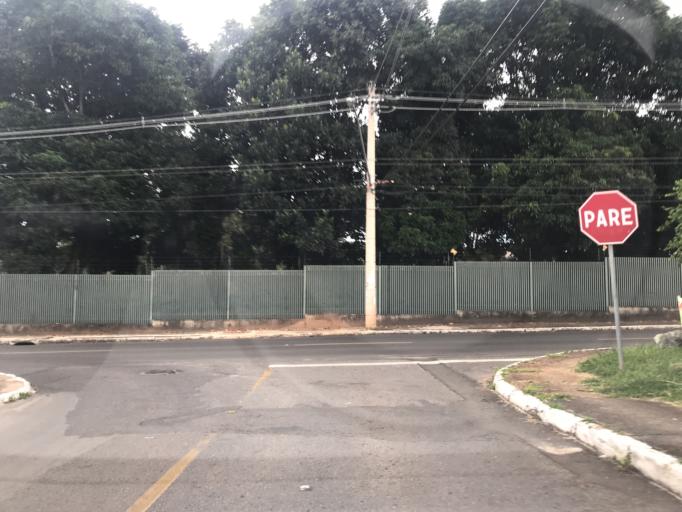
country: BR
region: Federal District
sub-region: Brasilia
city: Brasilia
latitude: -15.7196
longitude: -47.8759
